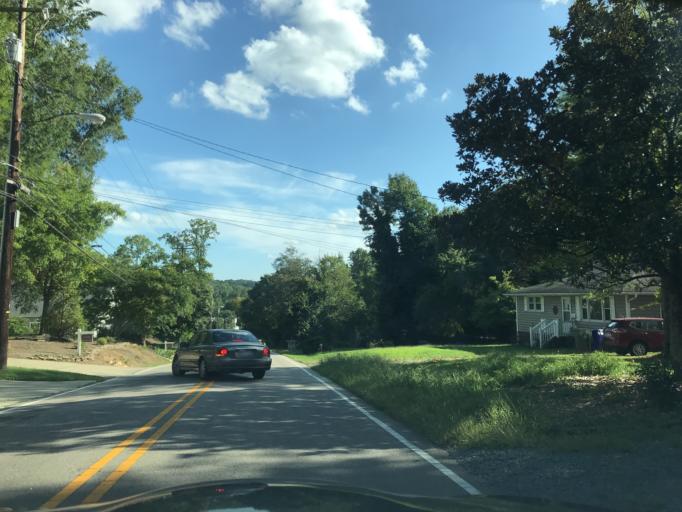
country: US
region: North Carolina
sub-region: Orange County
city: Carrboro
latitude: 35.9056
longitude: -79.0725
